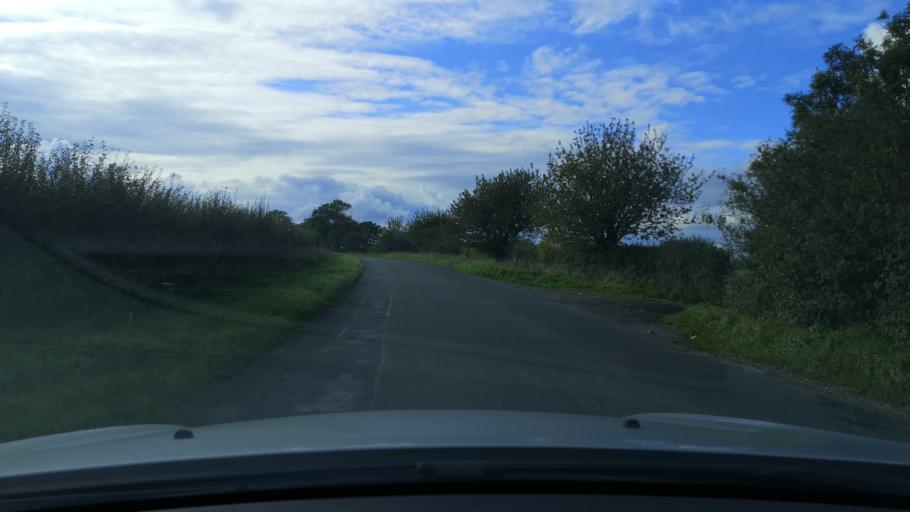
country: GB
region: England
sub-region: East Riding of Yorkshire
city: Walkington
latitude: 53.8260
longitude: -0.5196
